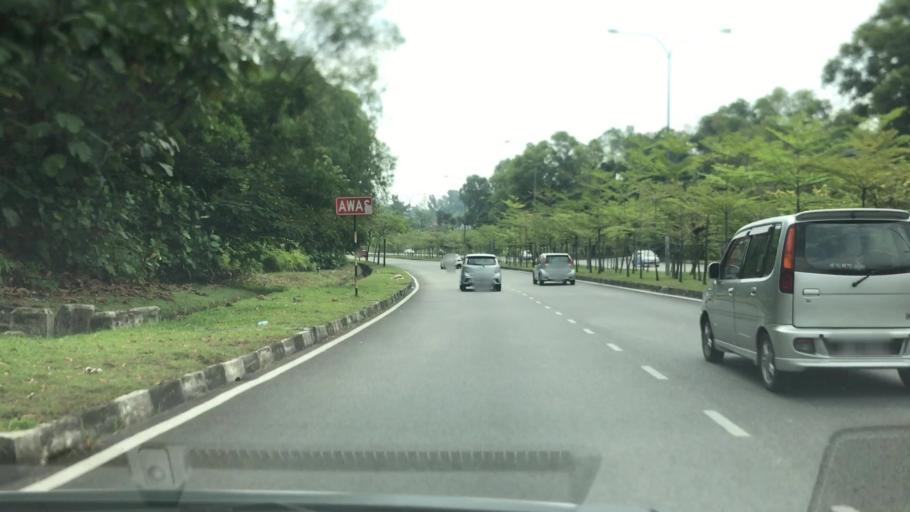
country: MY
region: Putrajaya
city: Putrajaya
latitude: 3.0061
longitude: 101.6694
